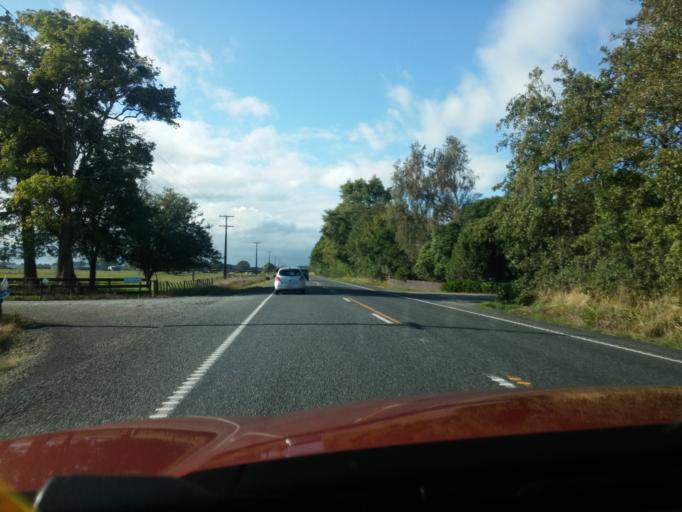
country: NZ
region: Waikato
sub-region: Hauraki District
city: Paeroa
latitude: -37.5646
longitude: 175.5499
